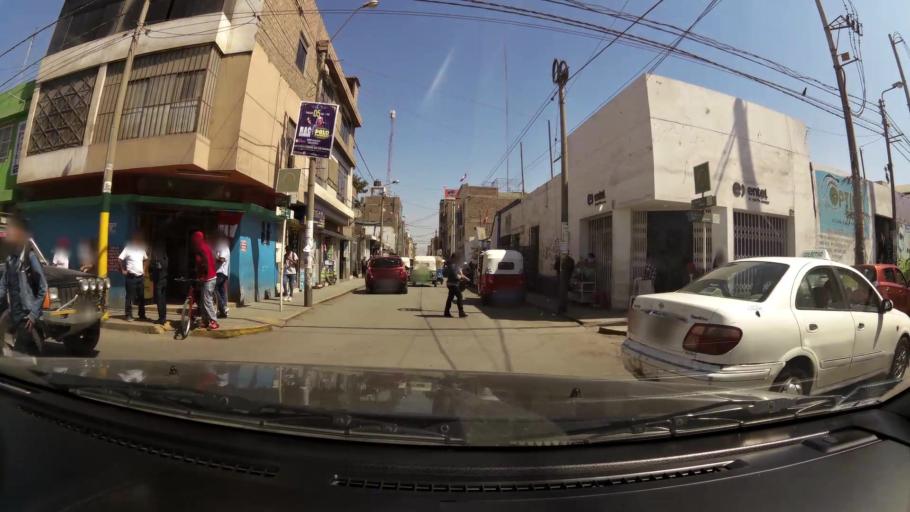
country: PE
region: Ica
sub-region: Provincia de Ica
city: Ica
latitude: -14.0623
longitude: -75.7291
